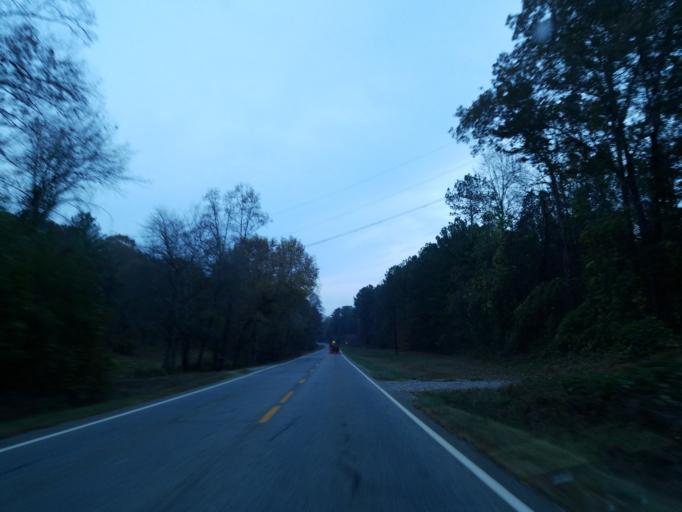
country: US
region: Georgia
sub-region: Pickens County
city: Jasper
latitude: 34.5174
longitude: -84.5679
